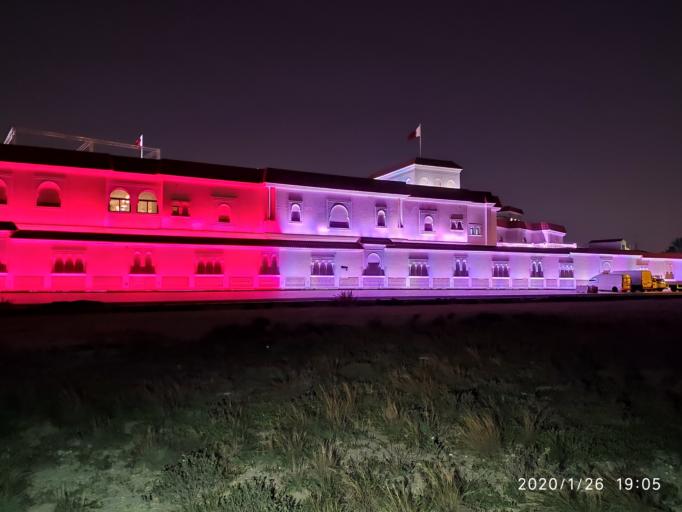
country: QA
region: Baladiyat ad Dawhah
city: Doha
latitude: 25.3261
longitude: 51.5015
